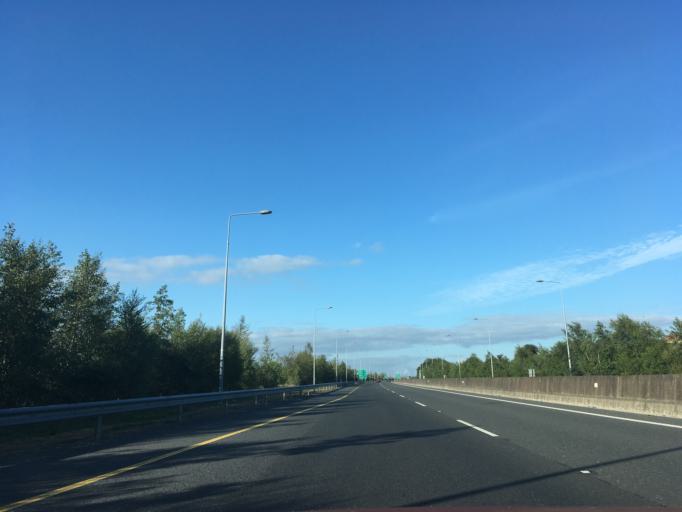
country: IE
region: Munster
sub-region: Waterford
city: Waterford
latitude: 52.2639
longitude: -7.1778
